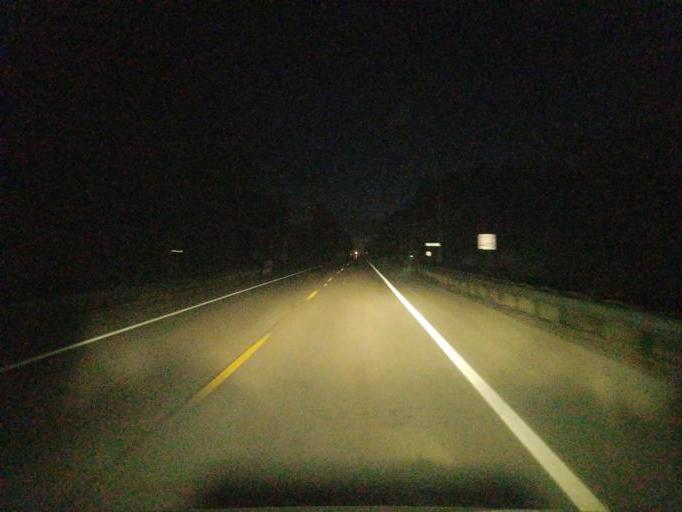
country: US
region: Ohio
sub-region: Geauga County
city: Middlefield
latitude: 41.5275
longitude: -81.0517
